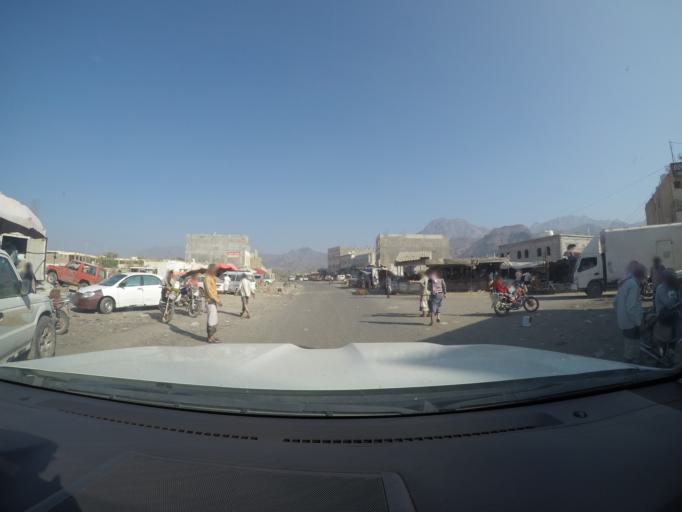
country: YE
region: Lahij
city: Habil ar Raydah
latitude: 13.6461
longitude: 44.8573
